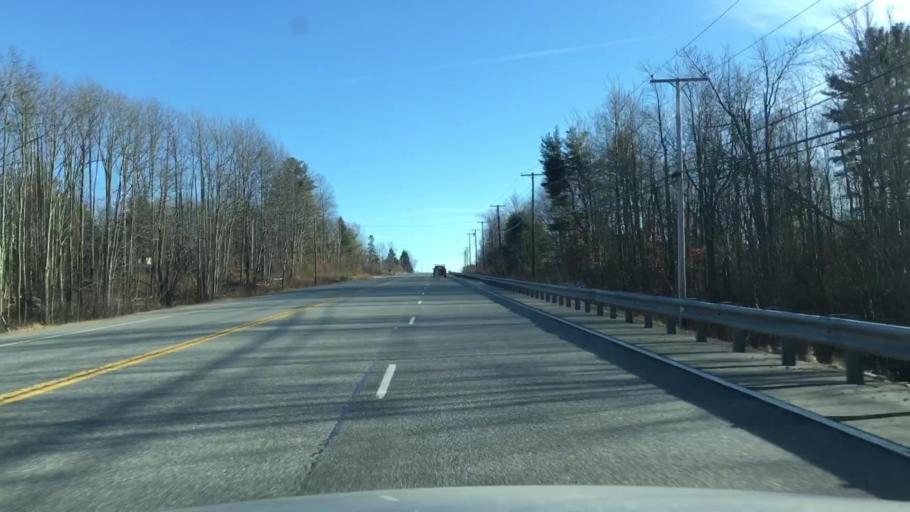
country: US
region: Maine
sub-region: Hancock County
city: Dedham
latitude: 44.6297
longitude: -68.5399
